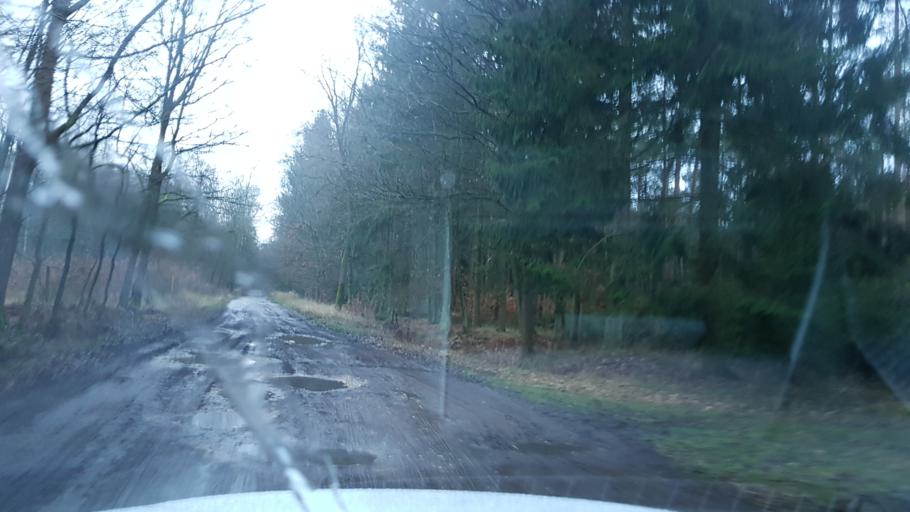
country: PL
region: West Pomeranian Voivodeship
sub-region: Powiat goleniowski
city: Osina
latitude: 53.5778
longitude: 15.0643
